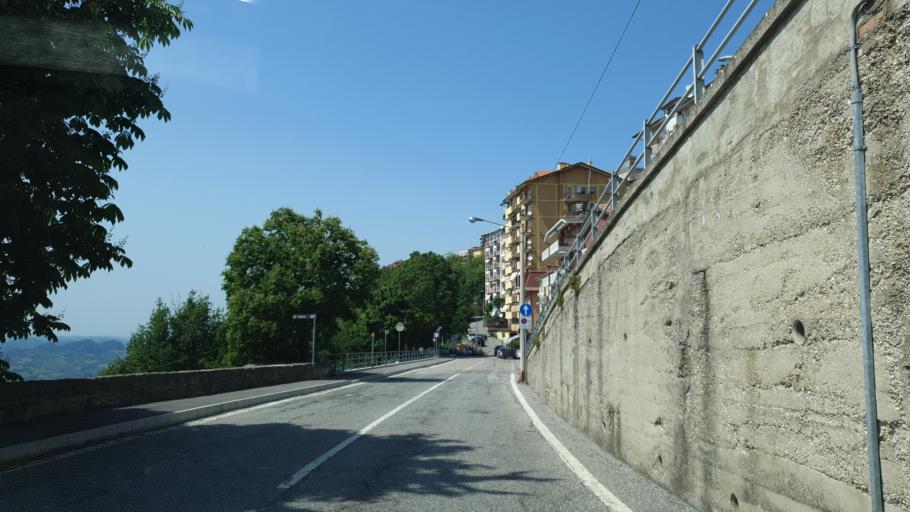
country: SM
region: San Marino
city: San Marino
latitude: 43.9322
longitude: 12.4467
